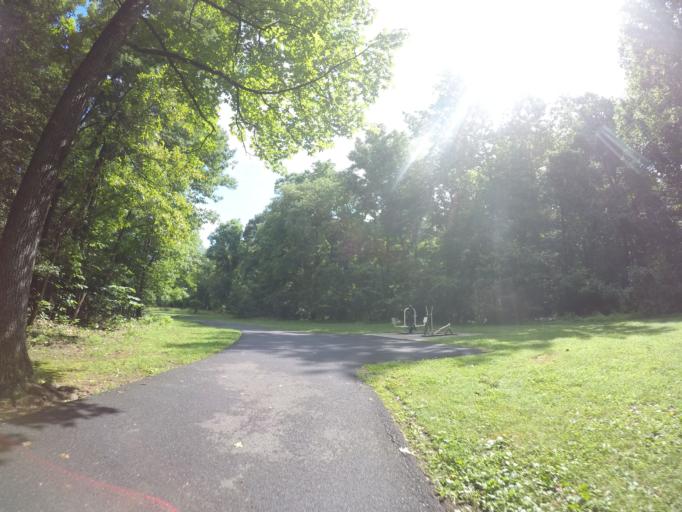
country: US
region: Maryland
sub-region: Prince George's County
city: East Riverdale
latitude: 38.9726
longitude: -76.9200
